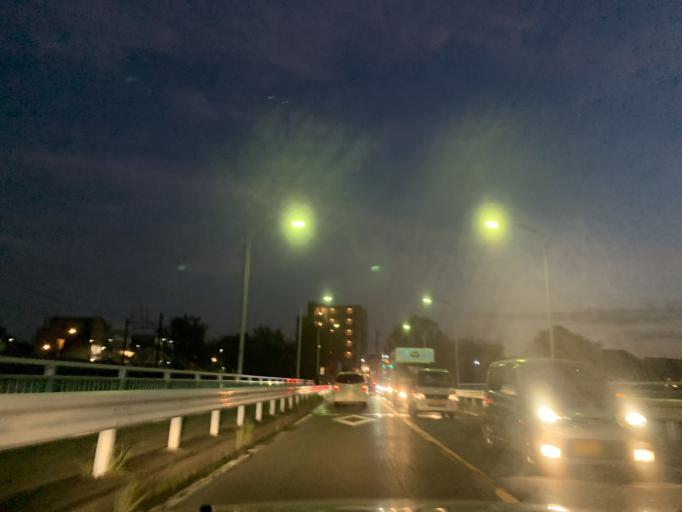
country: JP
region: Chiba
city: Noda
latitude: 35.9162
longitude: 139.9054
